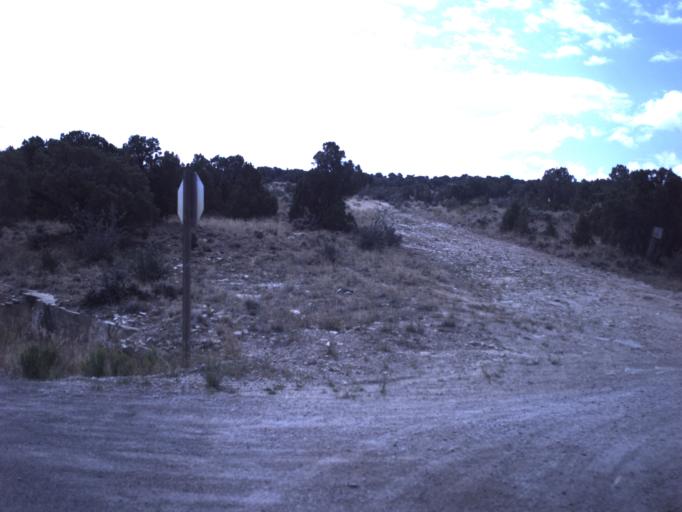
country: US
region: Utah
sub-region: Daggett County
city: Manila
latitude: 40.9390
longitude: -109.7125
